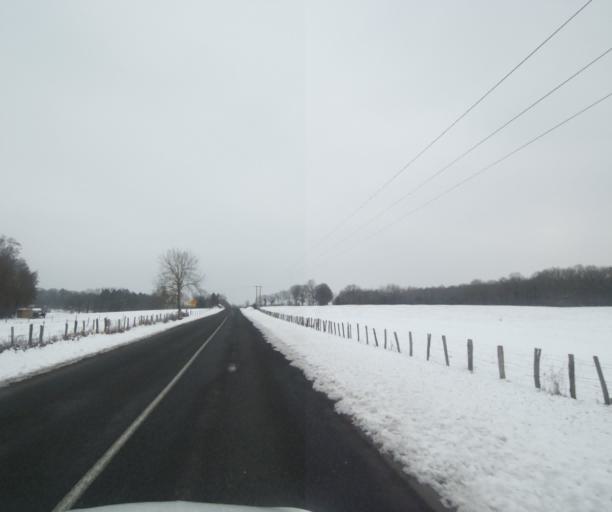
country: FR
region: Champagne-Ardenne
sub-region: Departement de la Haute-Marne
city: Villiers-en-Lieu
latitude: 48.6125
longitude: 4.8873
